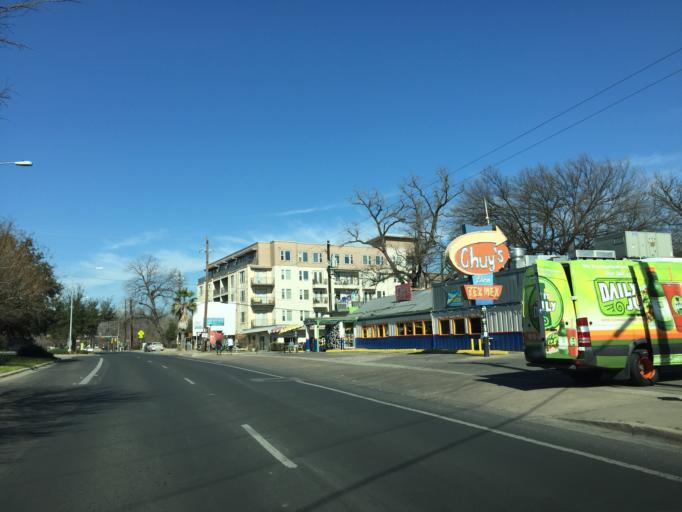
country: US
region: Texas
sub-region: Travis County
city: Austin
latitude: 30.2634
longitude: -97.7631
